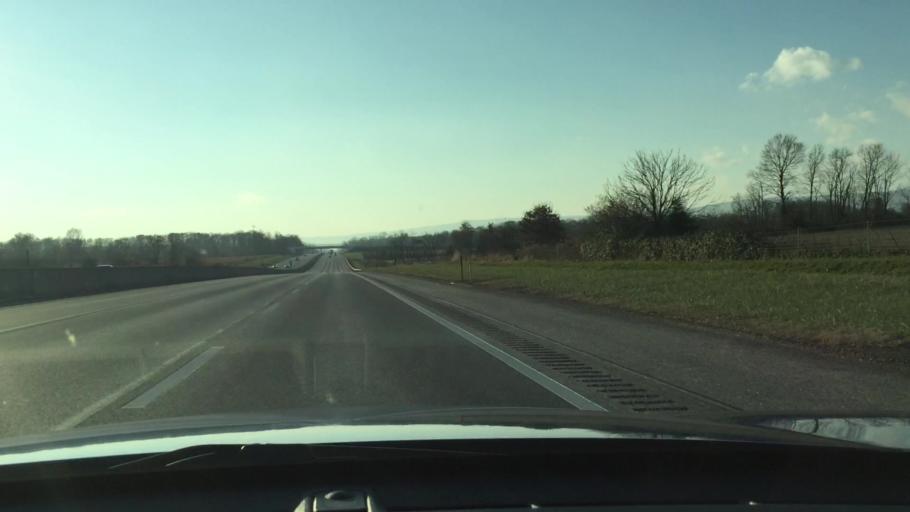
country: US
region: Pennsylvania
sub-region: Cumberland County
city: Newville
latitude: 40.1986
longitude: -77.3996
